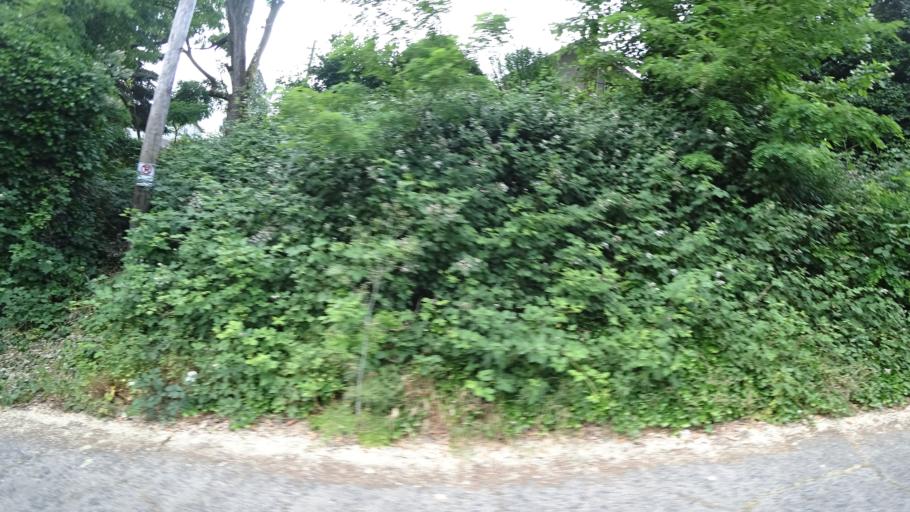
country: US
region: Oregon
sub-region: Washington County
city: West Haven
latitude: 45.5837
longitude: -122.7467
